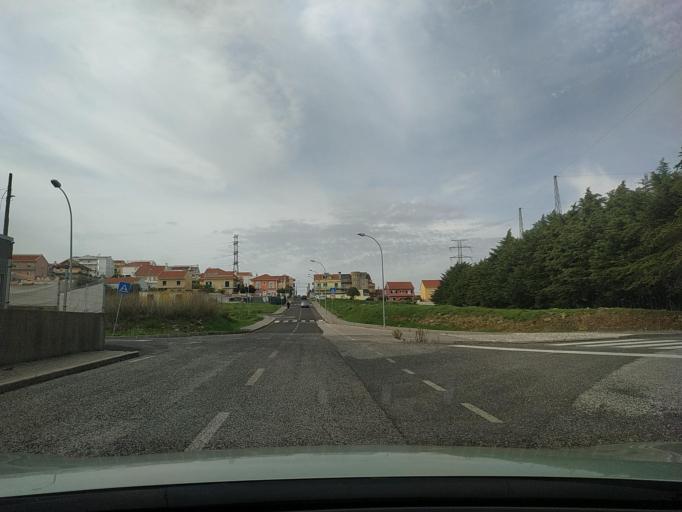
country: PT
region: Lisbon
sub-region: Sintra
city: Belas
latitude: 38.7770
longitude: -9.2402
